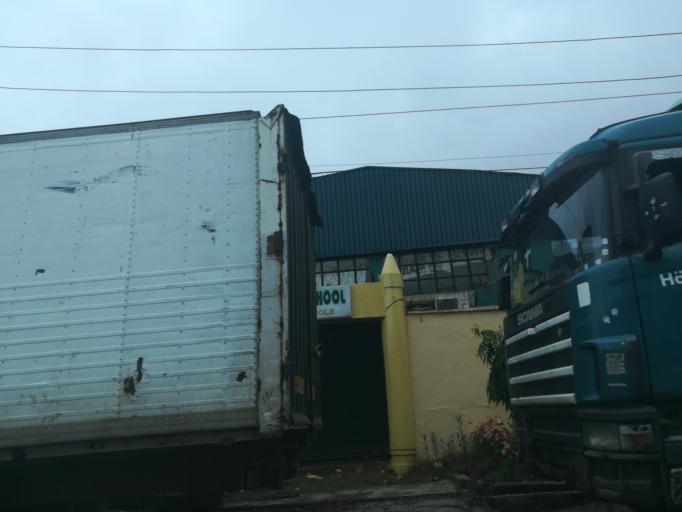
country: NG
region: Lagos
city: Agege
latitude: 6.6149
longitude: 3.3402
